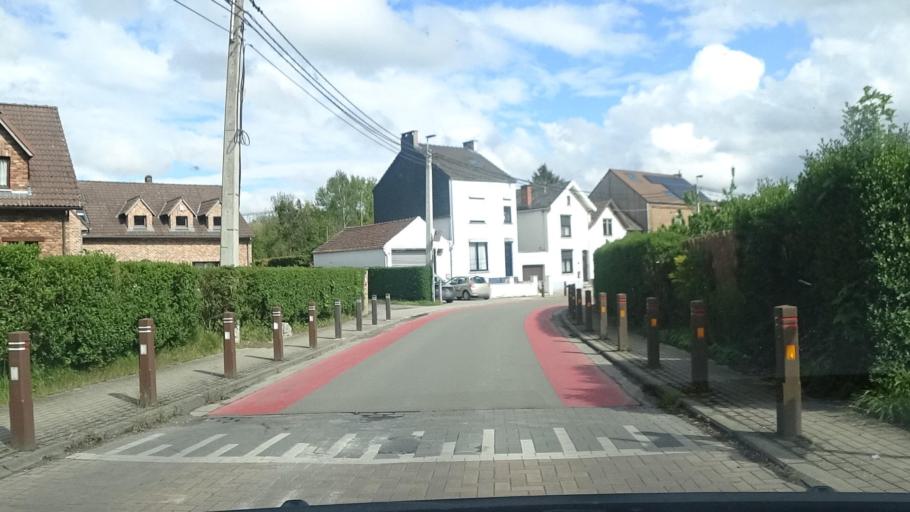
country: BE
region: Wallonia
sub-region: Province du Brabant Wallon
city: Ottignies
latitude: 50.6584
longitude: 4.5739
